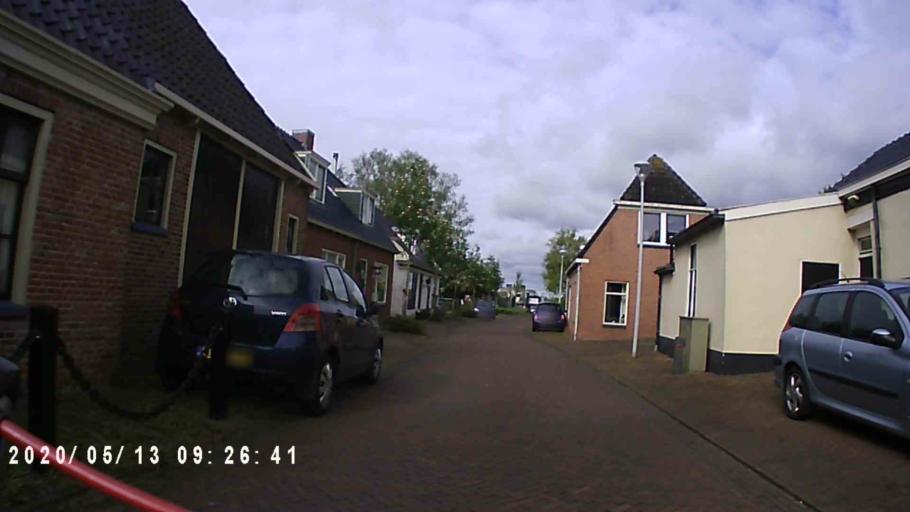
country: NL
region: Groningen
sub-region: Gemeente Zuidhorn
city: Noordhorn
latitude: 53.2594
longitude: 6.3957
